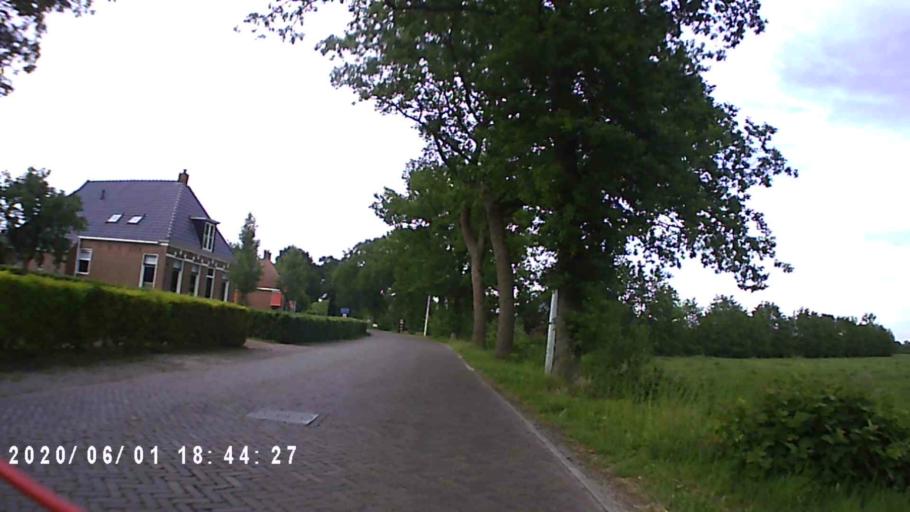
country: NL
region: Friesland
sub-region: Gemeente Tytsjerksteradiel
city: Eastermar
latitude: 53.1764
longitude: 6.0658
